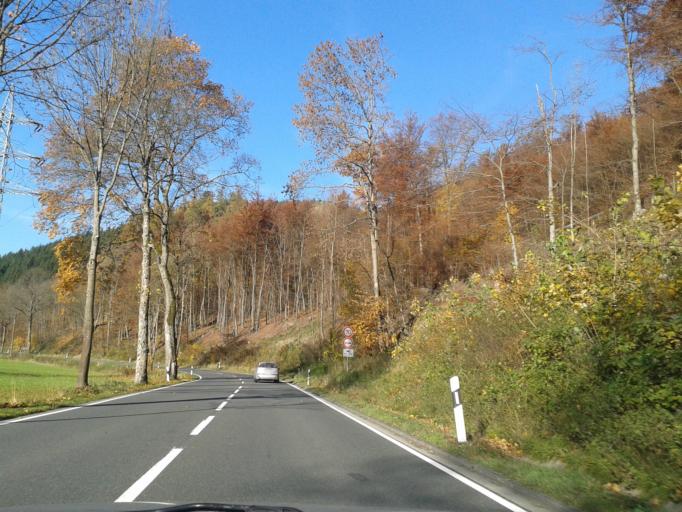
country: DE
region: North Rhine-Westphalia
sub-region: Regierungsbezirk Arnsberg
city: Bad Laasphe
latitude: 50.9413
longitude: 8.3787
